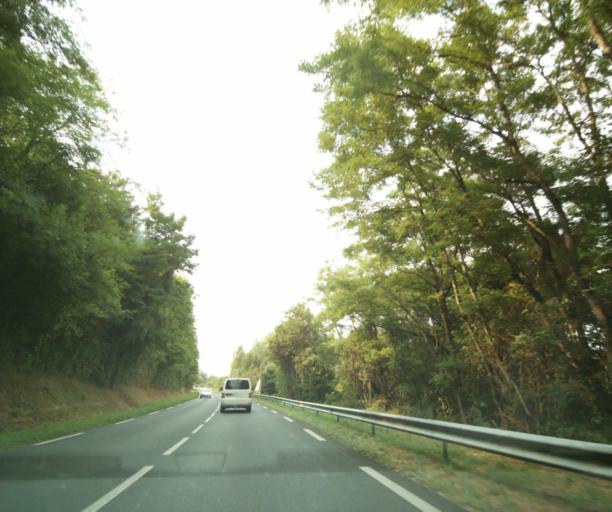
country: FR
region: Centre
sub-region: Departement de l'Indre
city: Clion
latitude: 46.9595
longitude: 1.2137
